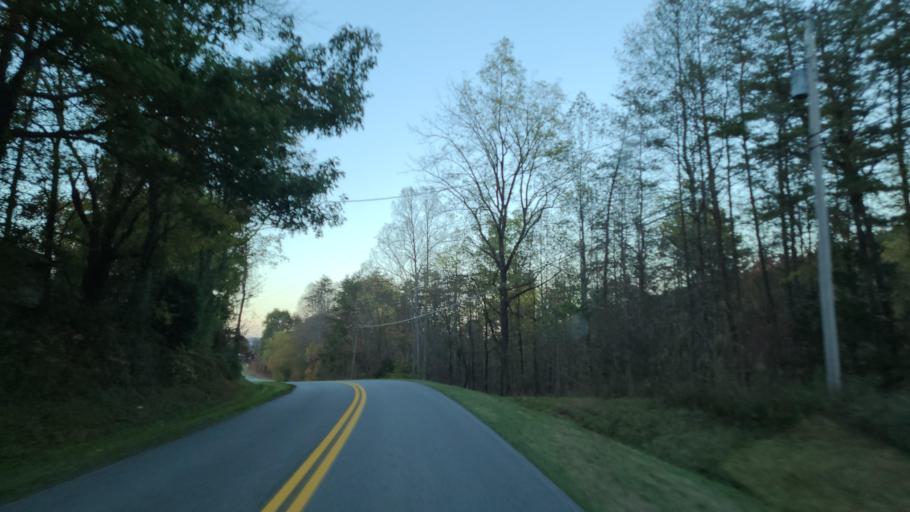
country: US
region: Georgia
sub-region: Union County
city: Blairsville
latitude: 34.9017
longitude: -83.8660
